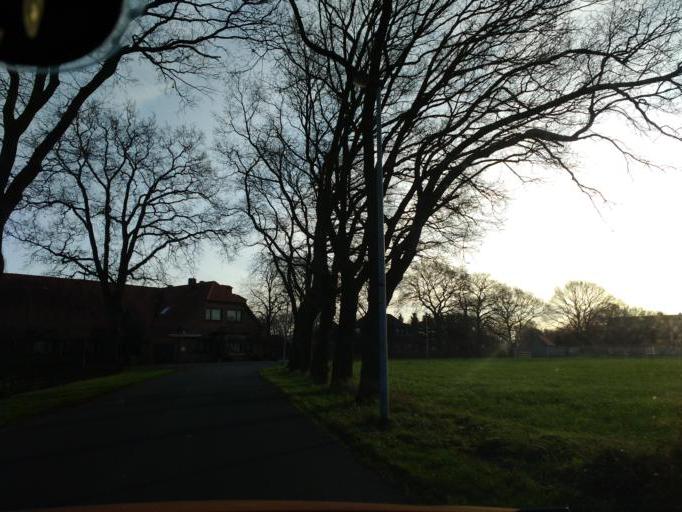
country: DE
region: Lower Saxony
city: Hatten
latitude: 53.1215
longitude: 8.3466
